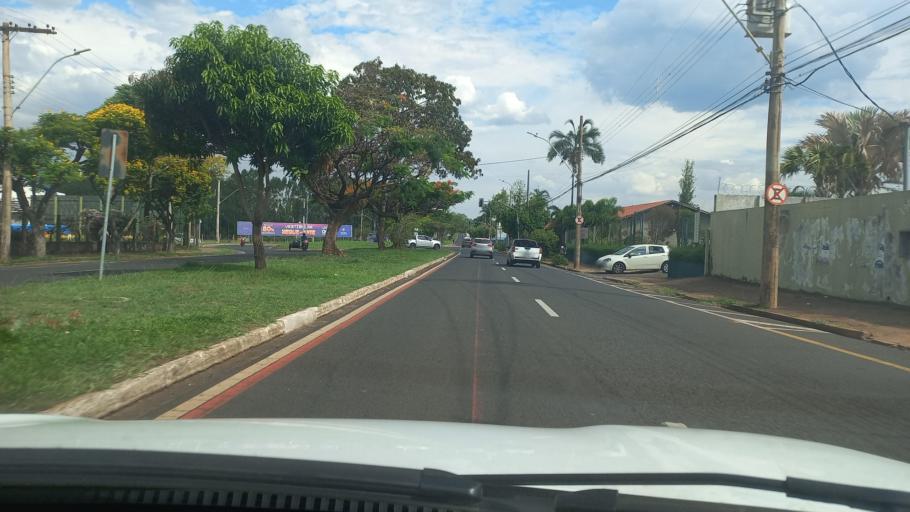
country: BR
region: Minas Gerais
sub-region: Uberaba
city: Uberaba
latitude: -19.7597
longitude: -47.9652
